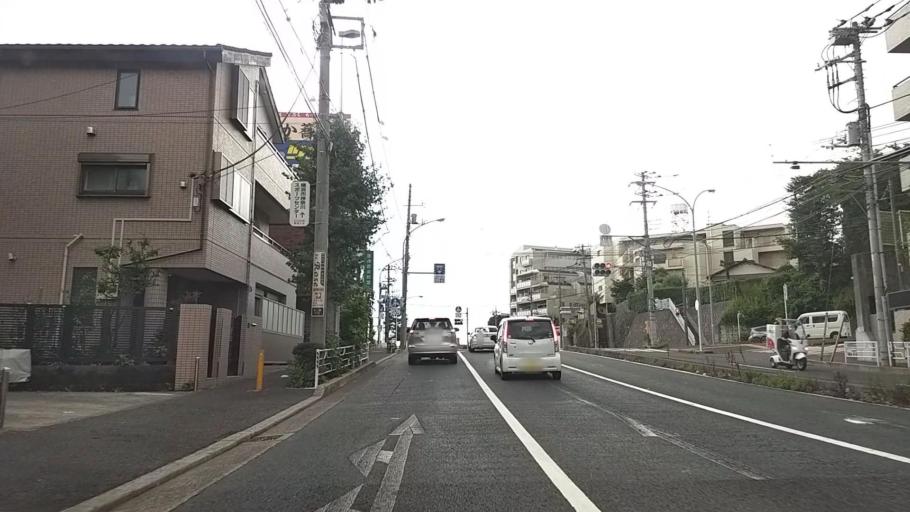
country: JP
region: Kanagawa
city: Yokohama
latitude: 35.4810
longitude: 139.6014
